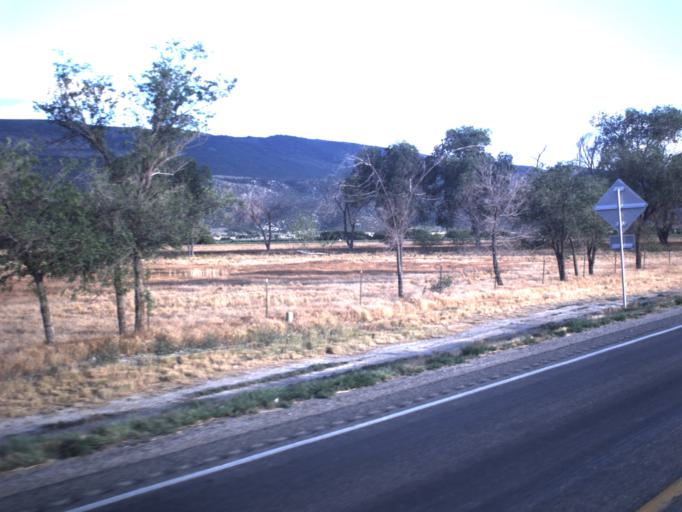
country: US
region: Utah
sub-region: Sanpete County
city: Ephraim
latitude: 39.3385
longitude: -111.5953
